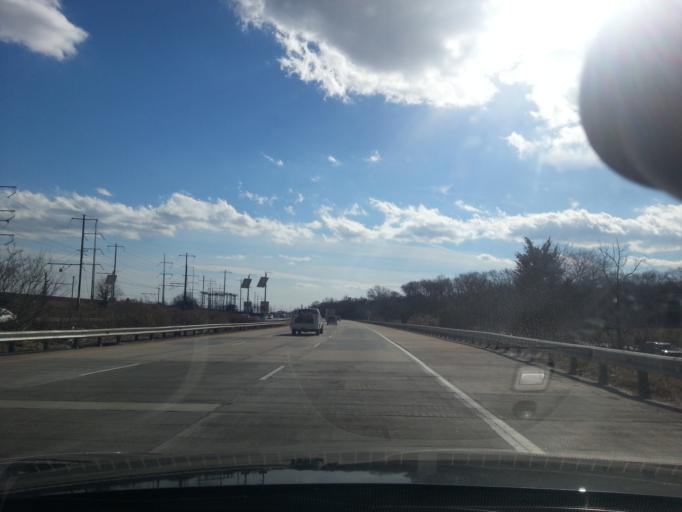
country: US
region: Delaware
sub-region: New Castle County
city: Bellefonte
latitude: 39.7746
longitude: -75.4812
